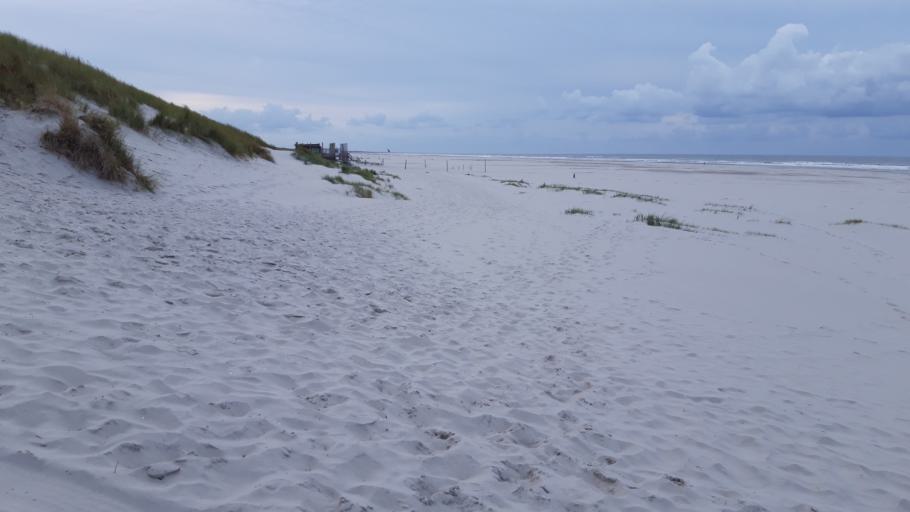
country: NL
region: Friesland
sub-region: Gemeente Ameland
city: Nes
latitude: 53.4590
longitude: 5.7580
